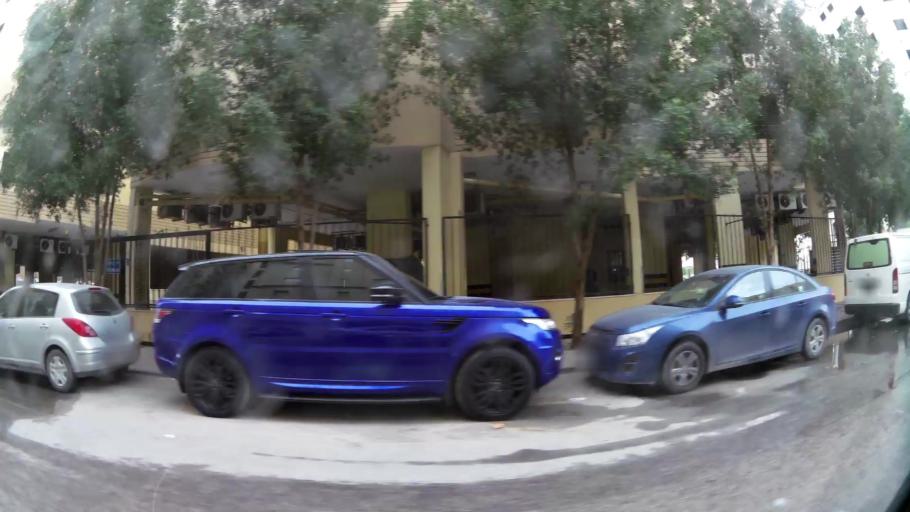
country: QA
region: Baladiyat ad Dawhah
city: Doha
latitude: 25.2810
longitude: 51.5096
